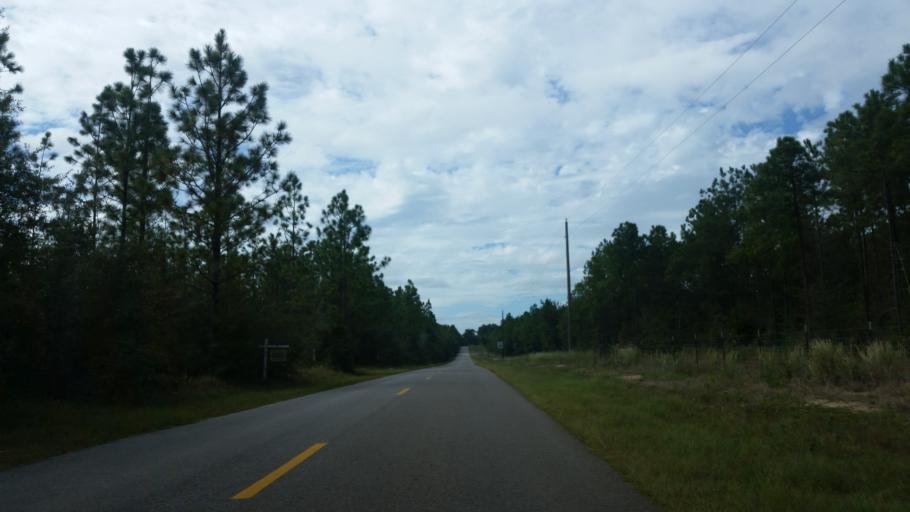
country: US
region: Florida
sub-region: Santa Rosa County
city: Point Baker
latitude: 30.7323
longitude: -87.0025
